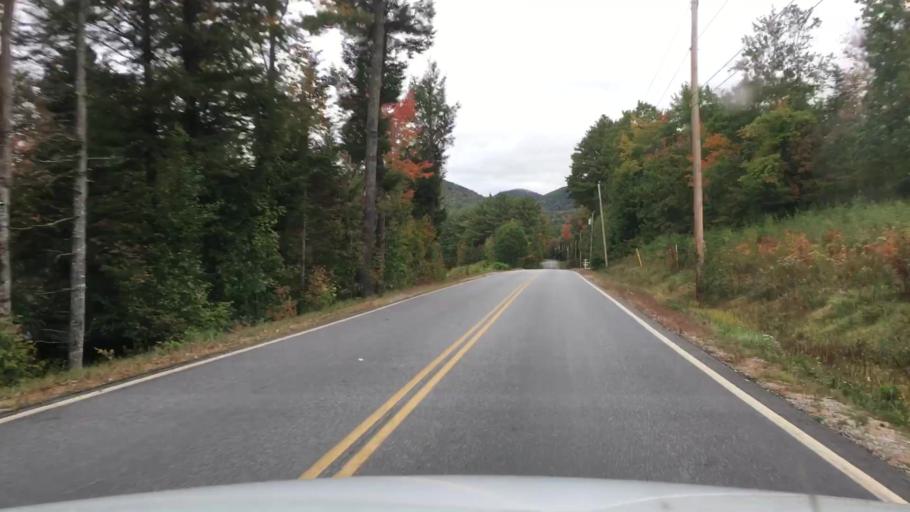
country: US
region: Maine
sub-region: Oxford County
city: Bethel
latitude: 44.2637
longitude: -70.7269
